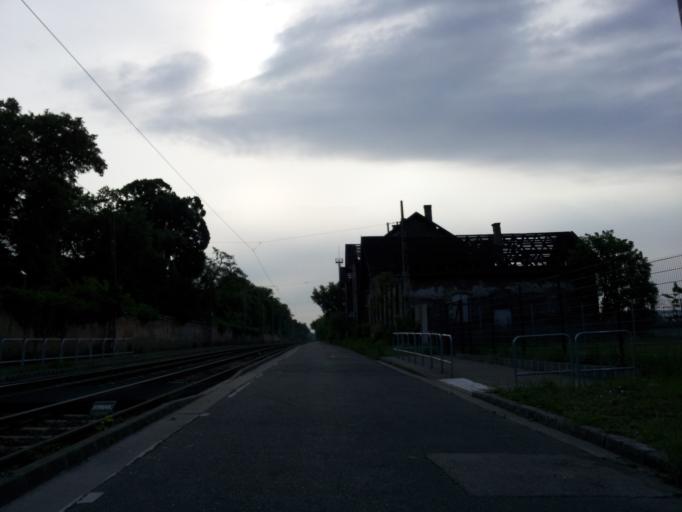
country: HU
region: Budapest
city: Budapest VIII. keruelet
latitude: 47.4916
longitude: 19.0912
